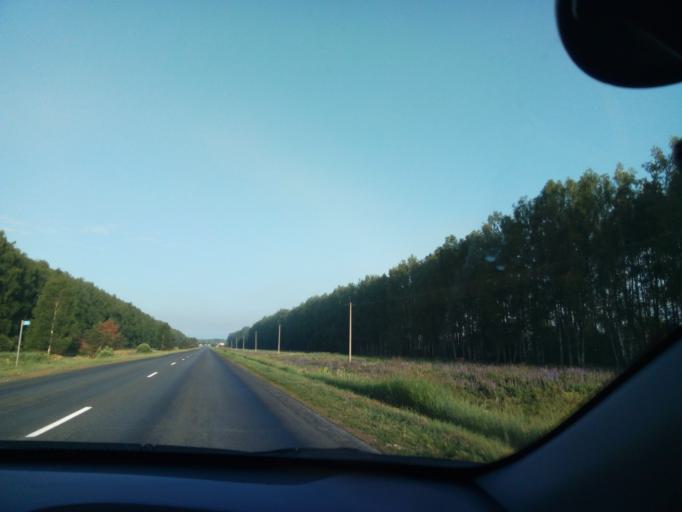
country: RU
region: Nizjnij Novgorod
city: Voznesenskoye
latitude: 54.8591
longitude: 42.9136
